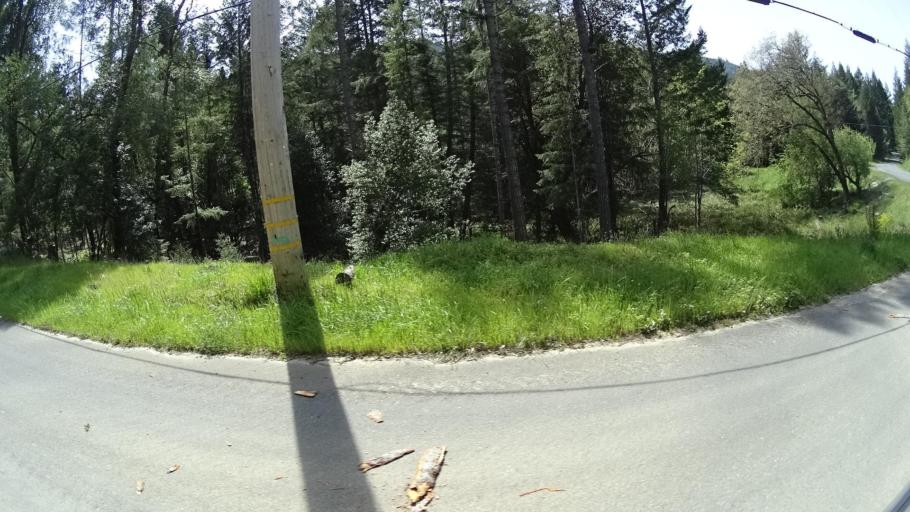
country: US
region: California
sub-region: Humboldt County
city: Redway
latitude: 40.3734
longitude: -123.7380
